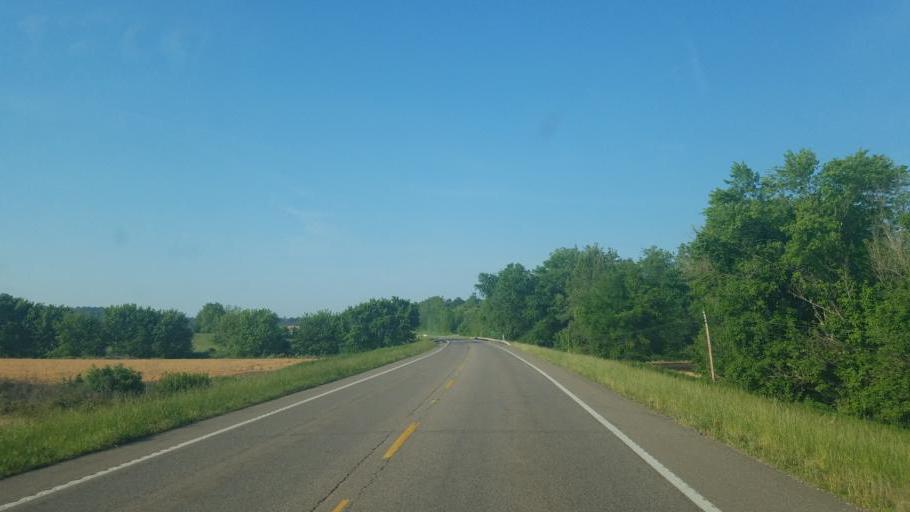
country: US
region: West Virginia
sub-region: Mason County
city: New Haven
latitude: 39.1018
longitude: -81.9249
